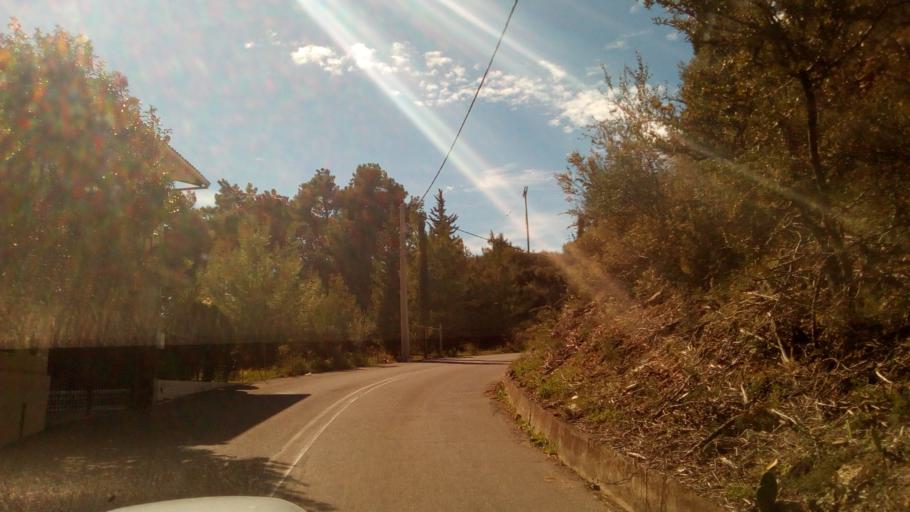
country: GR
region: West Greece
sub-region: Nomos Aitolias kai Akarnanias
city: Antirrio
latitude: 38.3684
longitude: 21.7785
